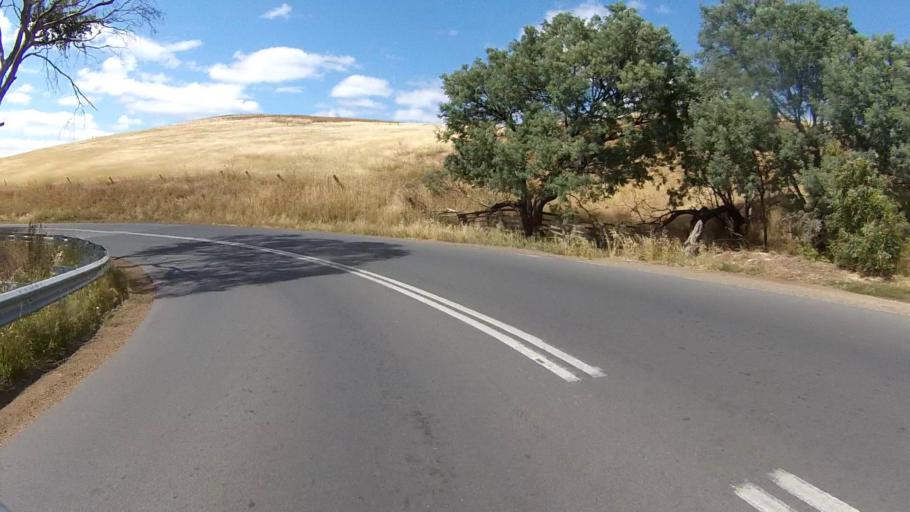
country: AU
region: Tasmania
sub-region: Brighton
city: Bridgewater
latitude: -42.5691
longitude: 147.3881
